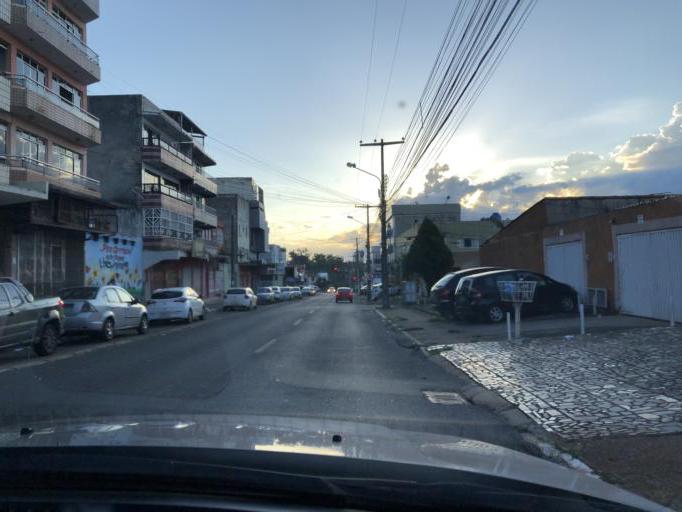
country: BR
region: Federal District
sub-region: Brasilia
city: Brasilia
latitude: -15.8471
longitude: -48.0473
